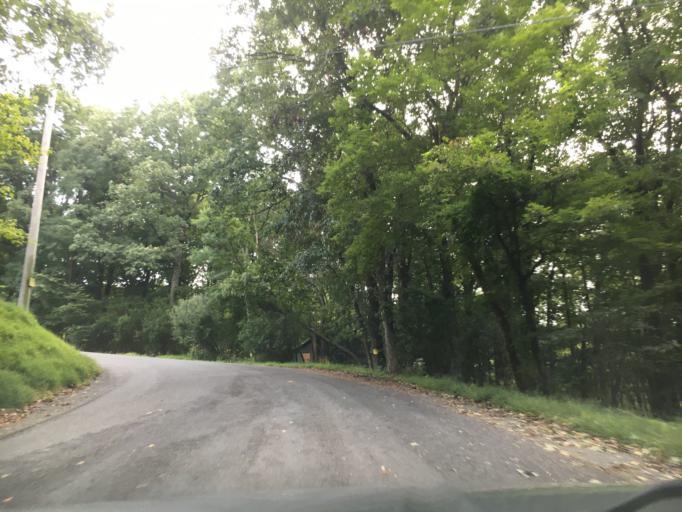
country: US
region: Pennsylvania
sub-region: Berks County
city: Topton
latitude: 40.6177
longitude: -75.7144
